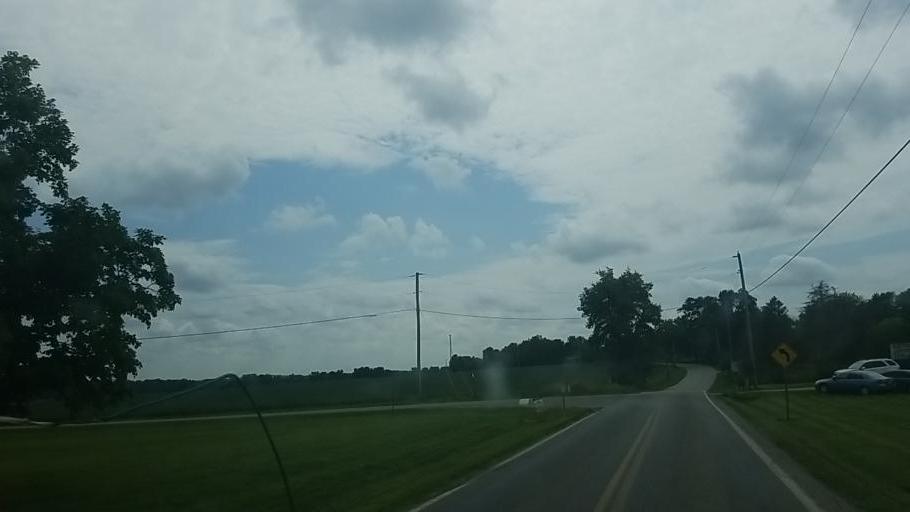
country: US
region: Ohio
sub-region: Pickaway County
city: Ashville
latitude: 39.7398
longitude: -82.8864
